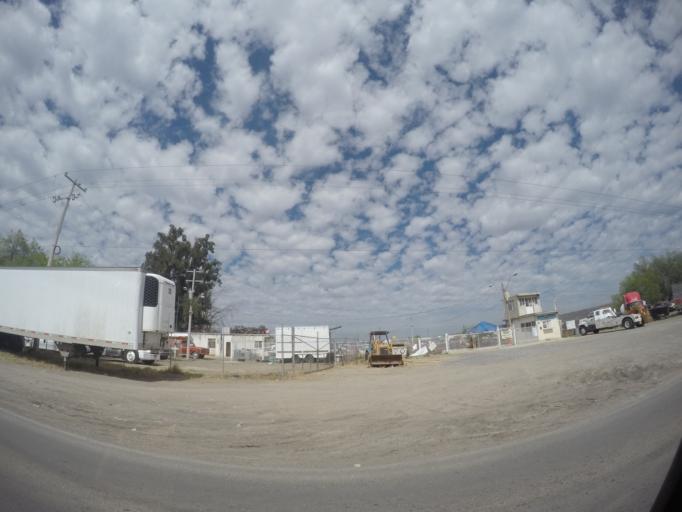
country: MX
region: Guanajuato
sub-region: Leon
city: Santa Ana
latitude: 21.0619
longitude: -101.6860
